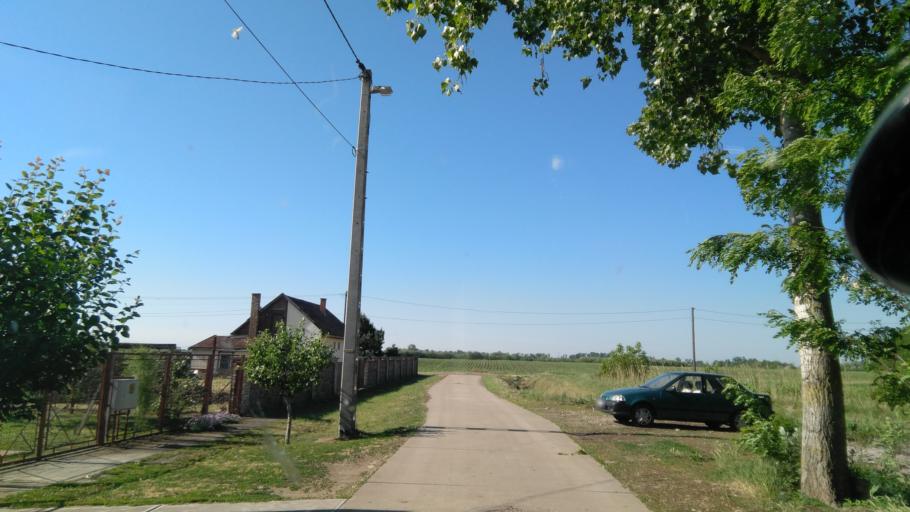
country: HU
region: Bekes
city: Elek
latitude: 46.5297
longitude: 21.2322
